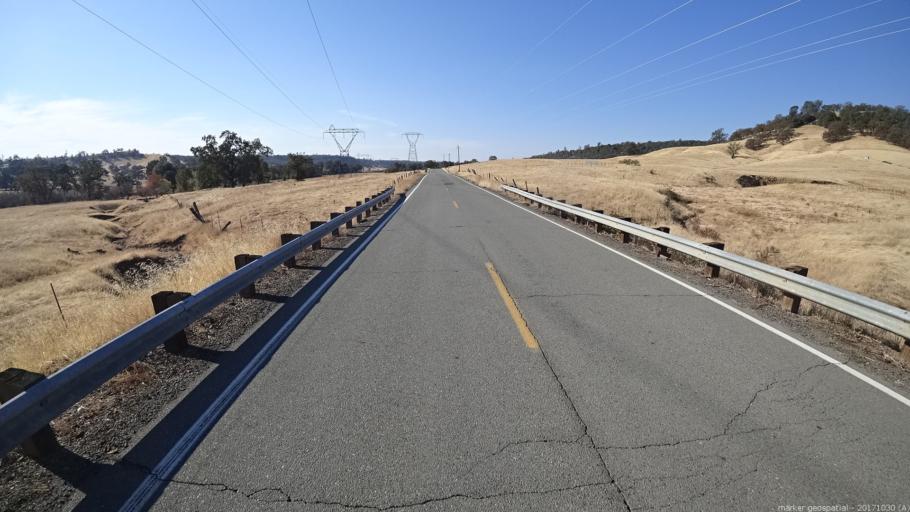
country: US
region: California
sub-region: Shasta County
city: Bella Vista
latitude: 40.6398
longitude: -122.0874
